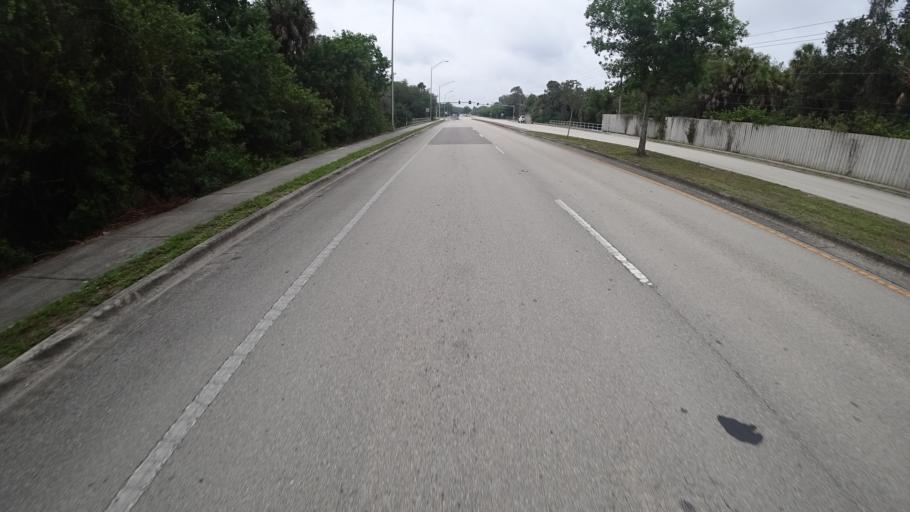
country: US
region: Florida
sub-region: Sarasota County
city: North Sarasota
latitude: 27.4194
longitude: -82.5052
